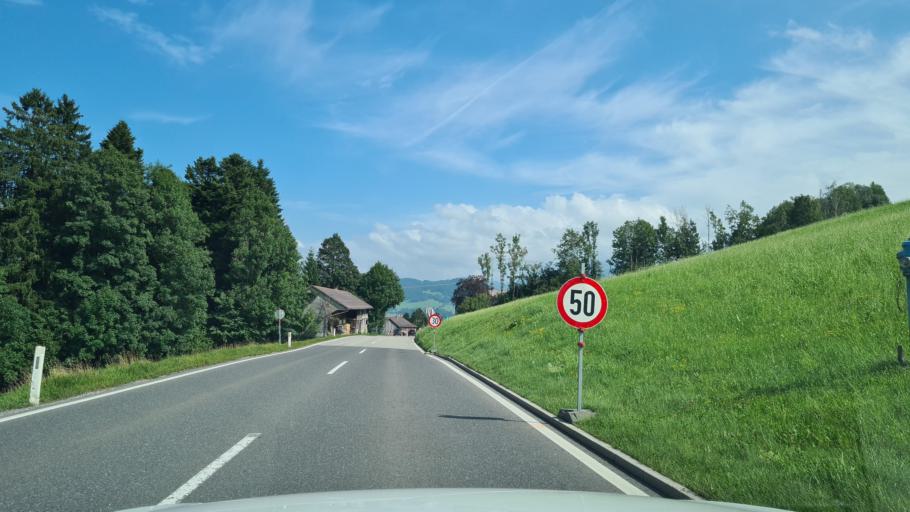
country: AT
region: Vorarlberg
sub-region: Politischer Bezirk Bregenz
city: Doren
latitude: 47.4580
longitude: 9.8638
